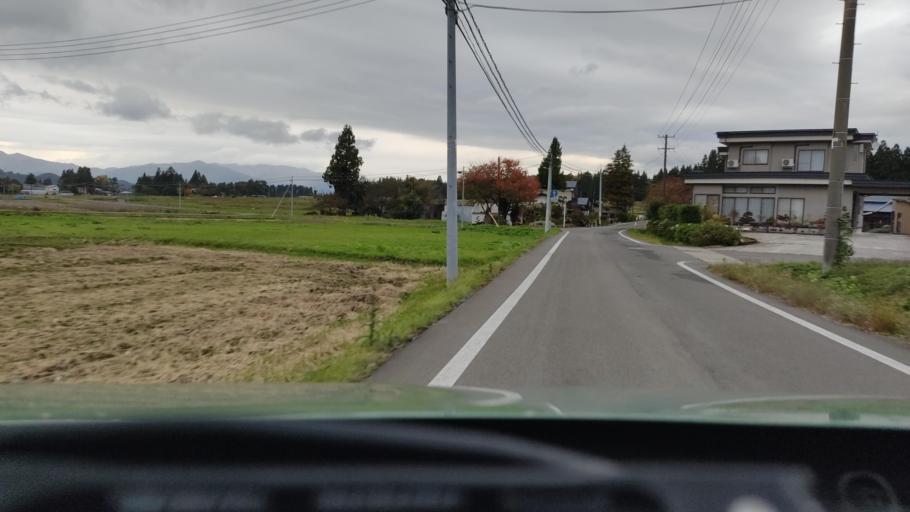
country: JP
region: Akita
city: Kakunodatemachi
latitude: 39.5673
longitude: 140.6112
